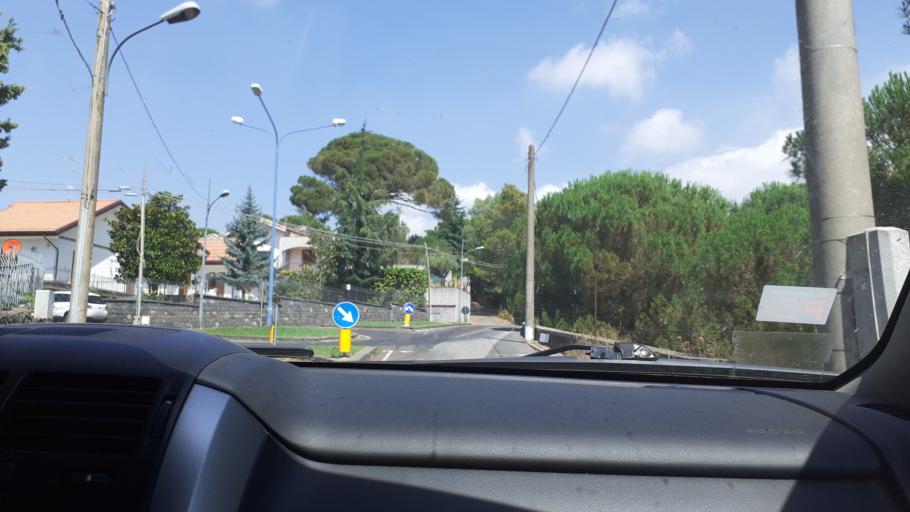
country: IT
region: Sicily
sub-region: Catania
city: Nicolosi
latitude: 37.6243
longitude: 15.0252
